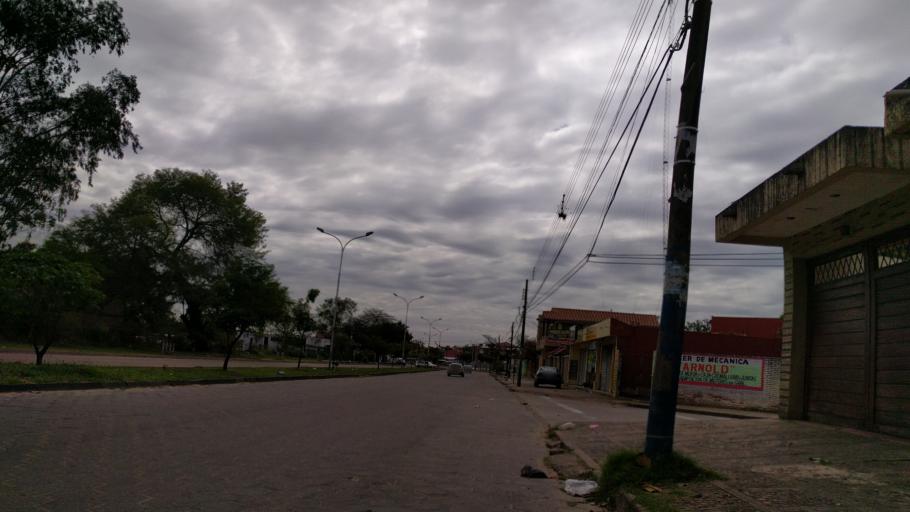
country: BO
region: Santa Cruz
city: Santa Cruz de la Sierra
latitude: -17.8129
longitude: -63.1964
